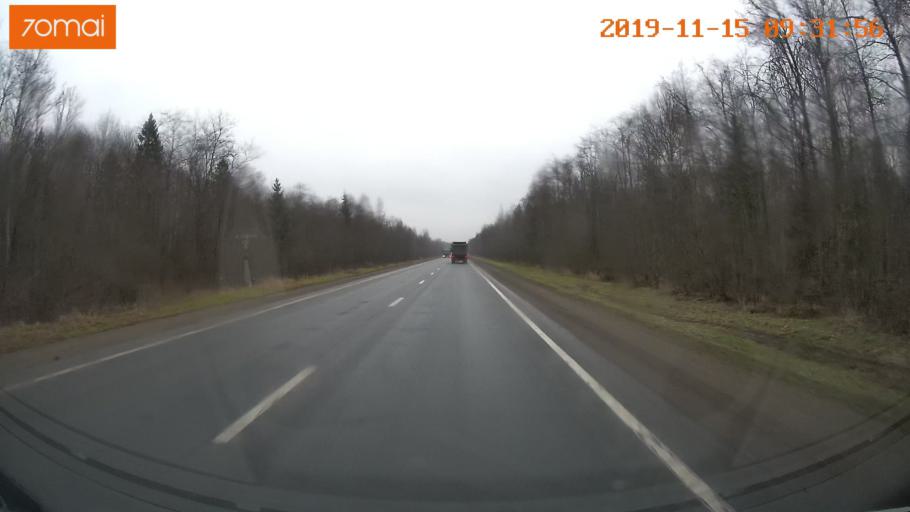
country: RU
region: Vologda
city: Sheksna
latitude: 59.2736
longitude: 38.3224
